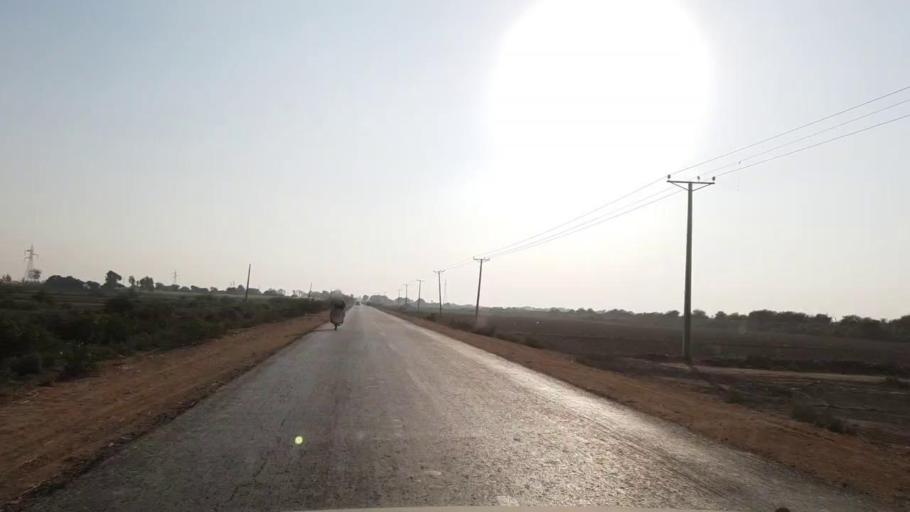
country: PK
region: Sindh
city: Mirpur Batoro
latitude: 24.7486
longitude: 68.2648
